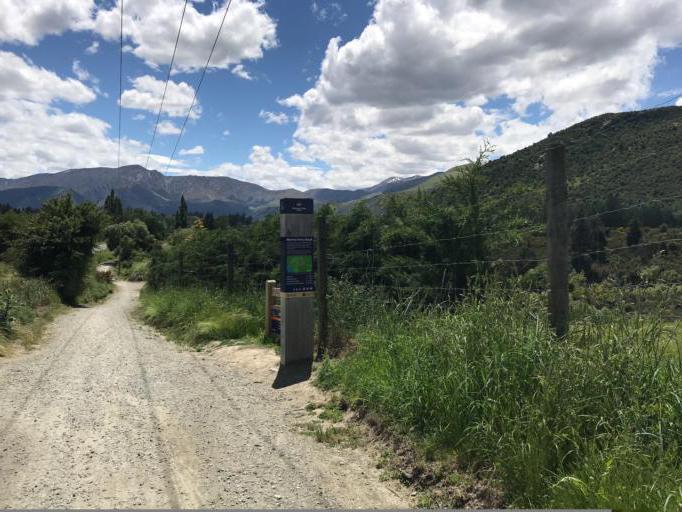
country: NZ
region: Otago
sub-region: Queenstown-Lakes District
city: Arrowtown
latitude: -44.9930
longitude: 168.8553
